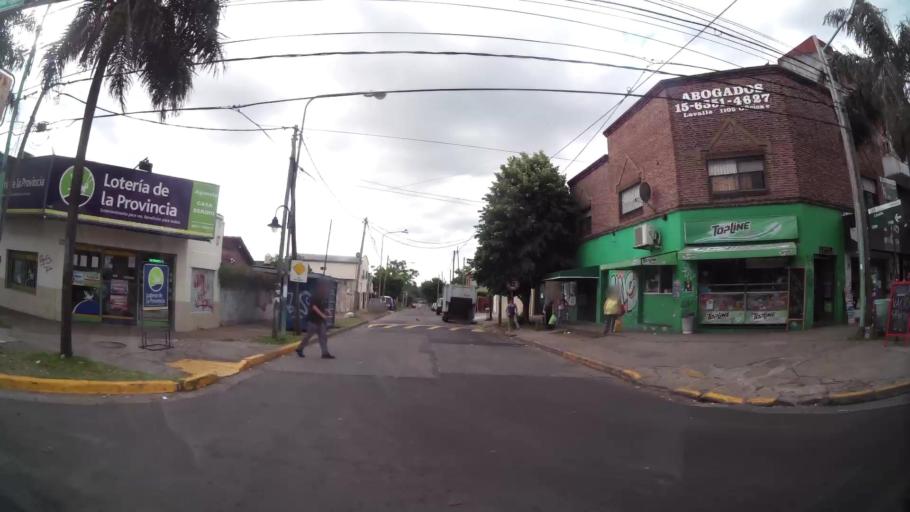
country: AR
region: Buenos Aires
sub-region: Partido de Tigre
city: Tigre
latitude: -34.4668
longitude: -58.6465
